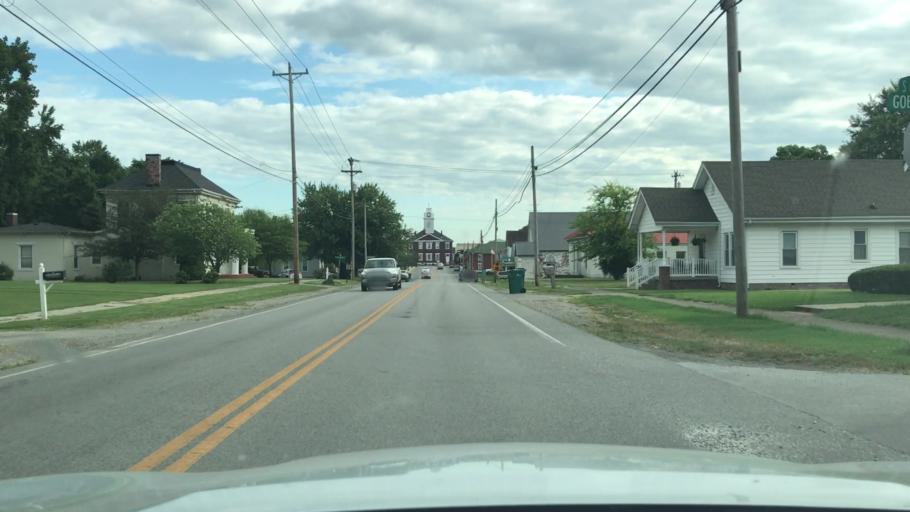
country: US
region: Kentucky
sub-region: Todd County
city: Elkton
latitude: 36.8064
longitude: -87.1550
